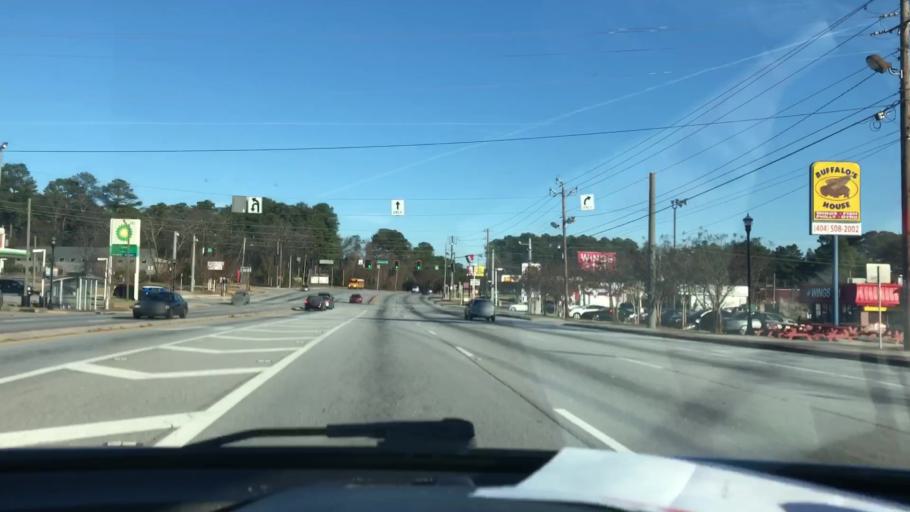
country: US
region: Georgia
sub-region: DeKalb County
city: Clarkston
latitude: 33.8010
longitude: -84.2073
